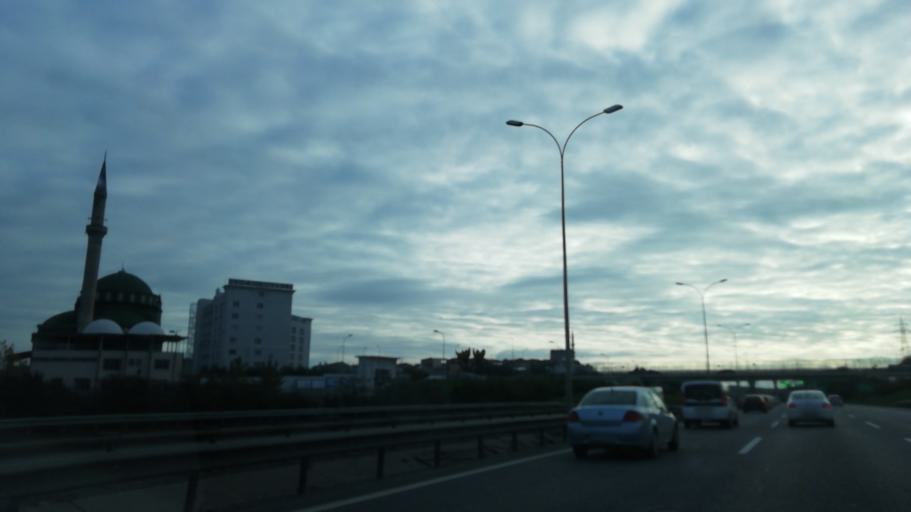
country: TR
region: Istanbul
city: Sultanbeyli
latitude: 40.9544
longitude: 29.2955
